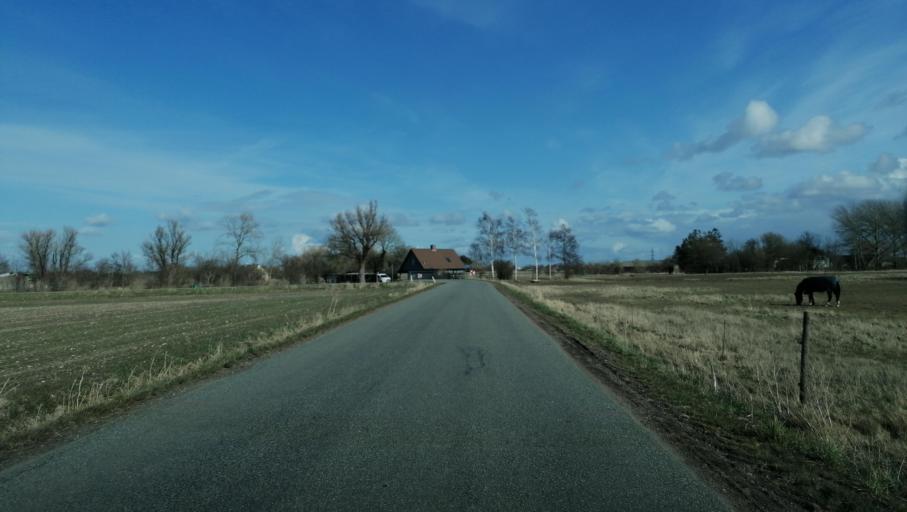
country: DK
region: Zealand
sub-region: Odsherred Kommune
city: Horve
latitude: 55.7486
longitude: 11.4802
